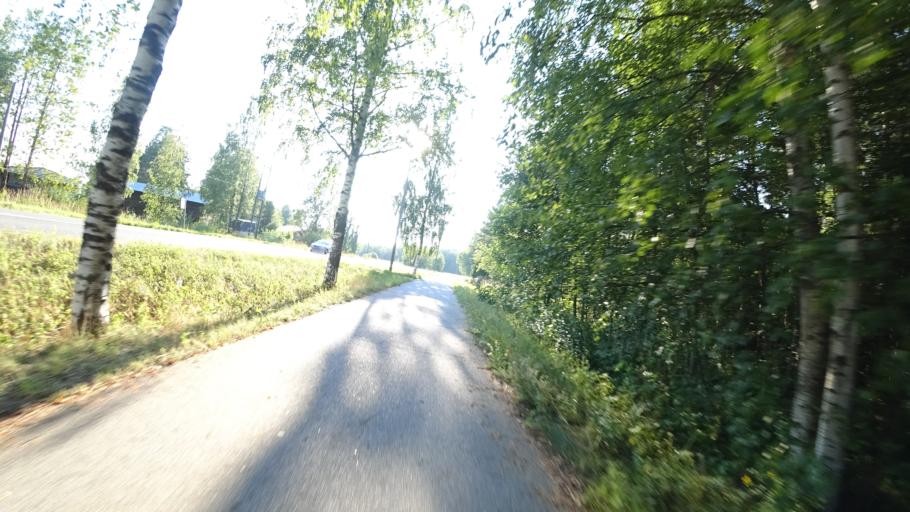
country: FI
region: Pirkanmaa
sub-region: Tampere
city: Nokia
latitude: 61.4680
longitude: 23.3990
